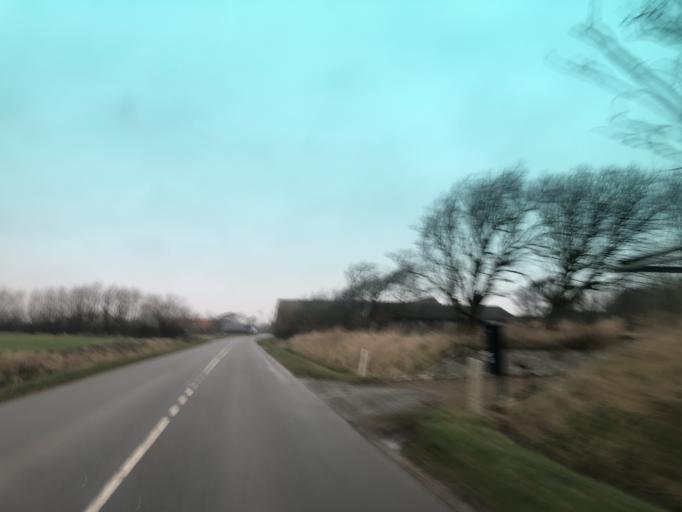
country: DK
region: North Denmark
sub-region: Thisted Kommune
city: Hurup
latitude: 56.7356
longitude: 8.4159
